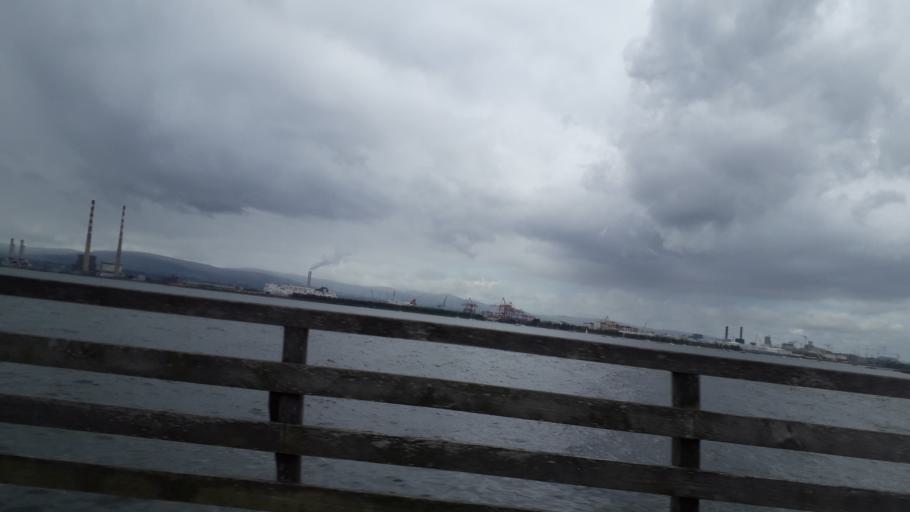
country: IE
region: Leinster
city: Dollymount
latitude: 53.3599
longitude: -6.1806
